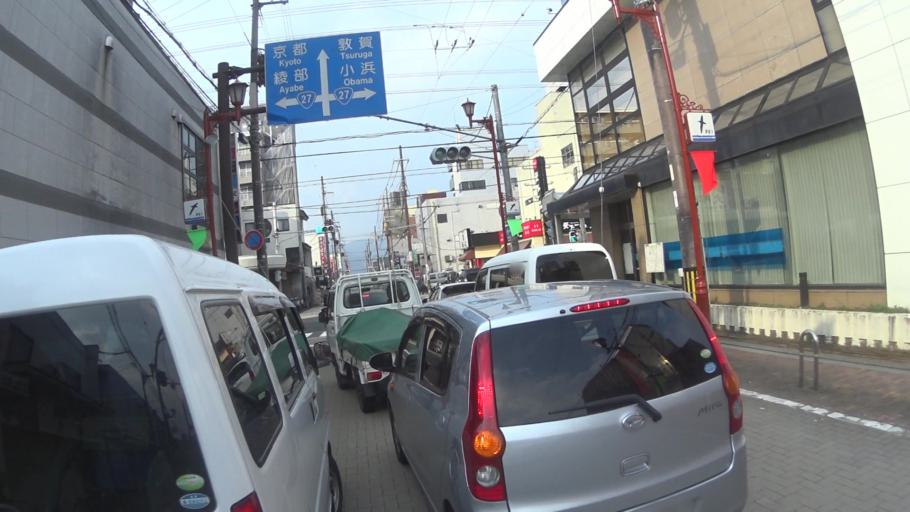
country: JP
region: Kyoto
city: Maizuru
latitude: 35.4748
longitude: 135.3954
